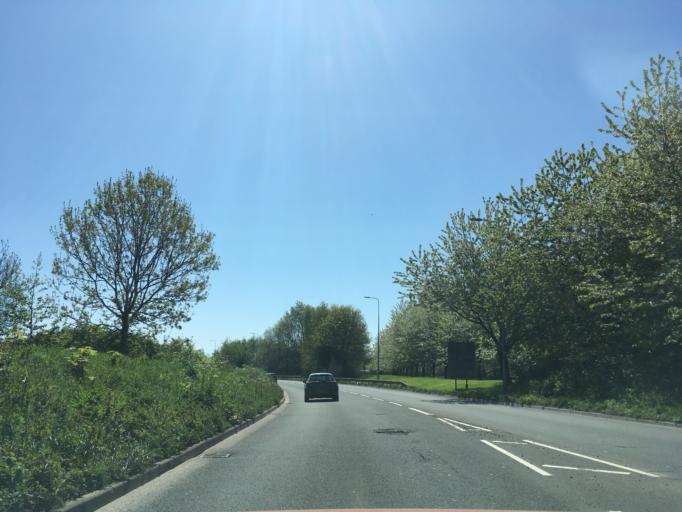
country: GB
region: Wales
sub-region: Cardiff
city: Cardiff
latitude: 51.4925
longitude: -3.1337
